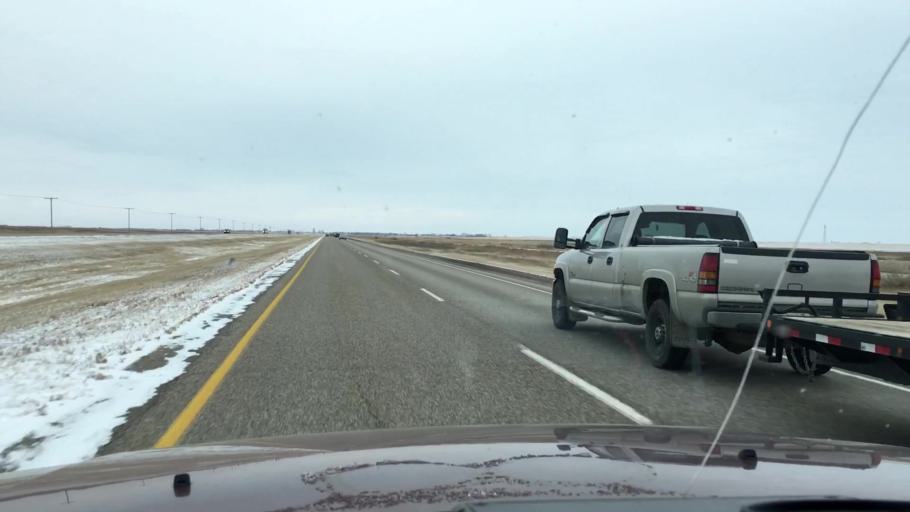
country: CA
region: Saskatchewan
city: Watrous
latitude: 51.0909
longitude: -105.8580
